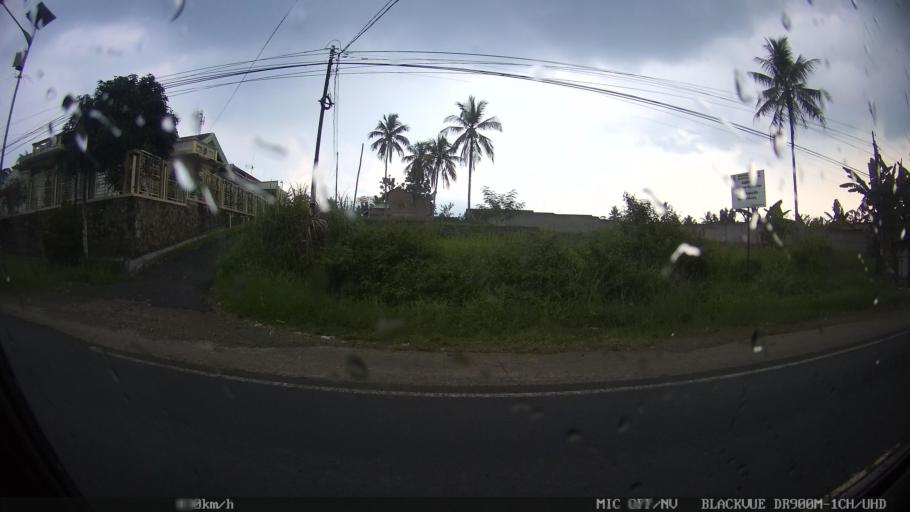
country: ID
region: Lampung
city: Gedongtataan
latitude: -5.3796
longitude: 105.1145
